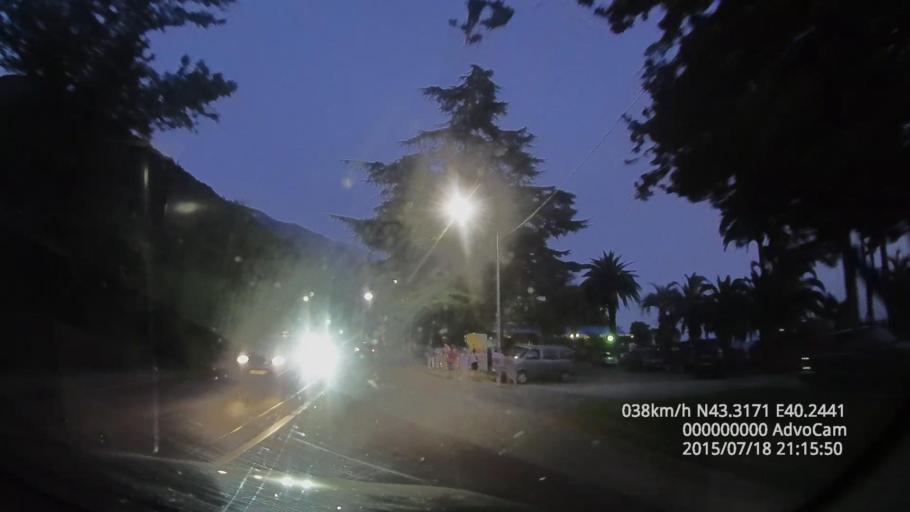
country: GE
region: Abkhazia
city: Gagra
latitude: 43.3170
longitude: 40.2443
